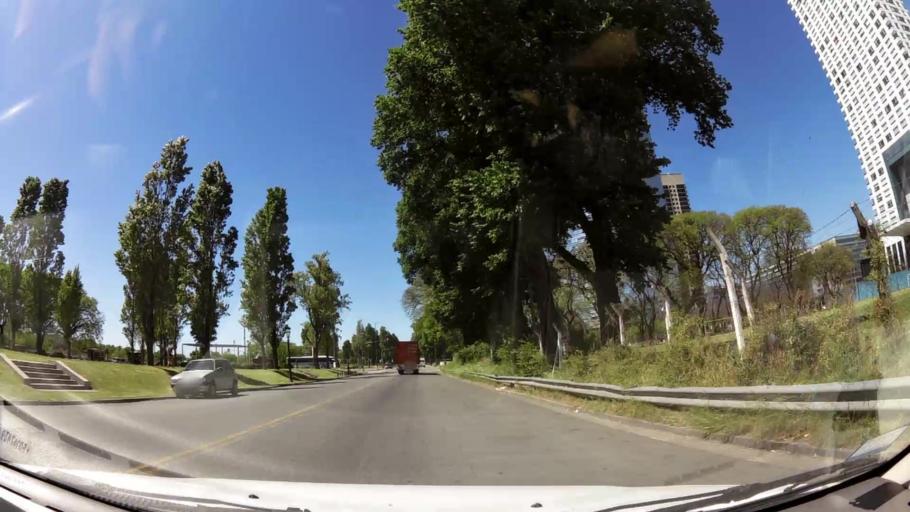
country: AR
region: Buenos Aires F.D.
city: Buenos Aires
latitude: -34.6039
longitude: -58.3619
